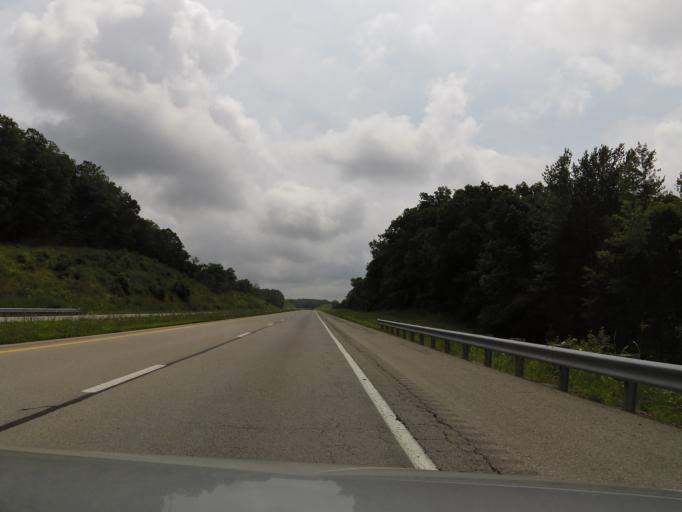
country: US
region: Kentucky
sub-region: Ohio County
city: Oak Grove
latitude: 37.3872
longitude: -86.6696
